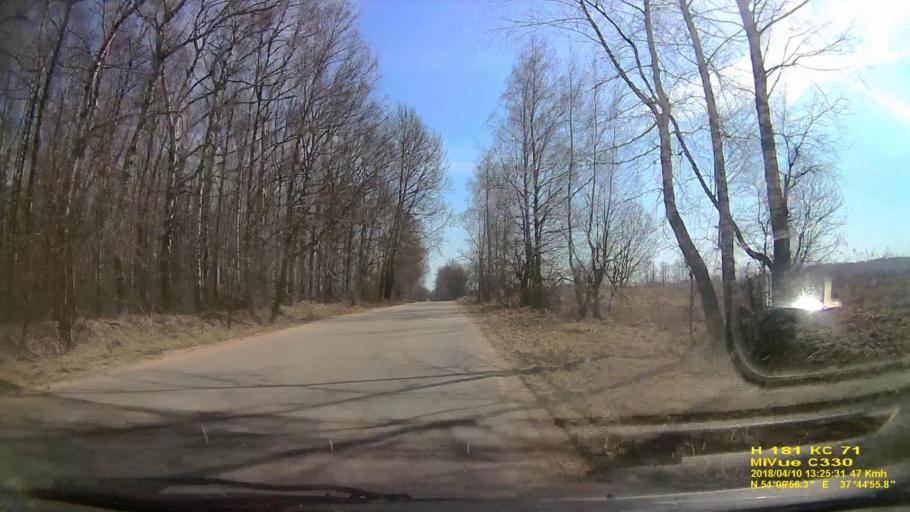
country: RU
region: Tula
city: Bolokhovo
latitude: 54.1656
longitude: 37.7489
